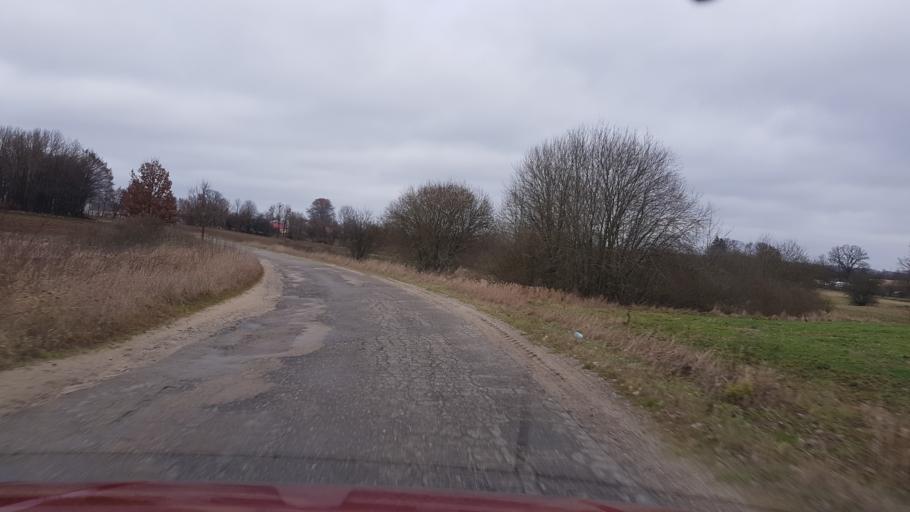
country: PL
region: Pomeranian Voivodeship
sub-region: Powiat bytowski
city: Tuchomie
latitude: 54.1597
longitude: 17.3422
